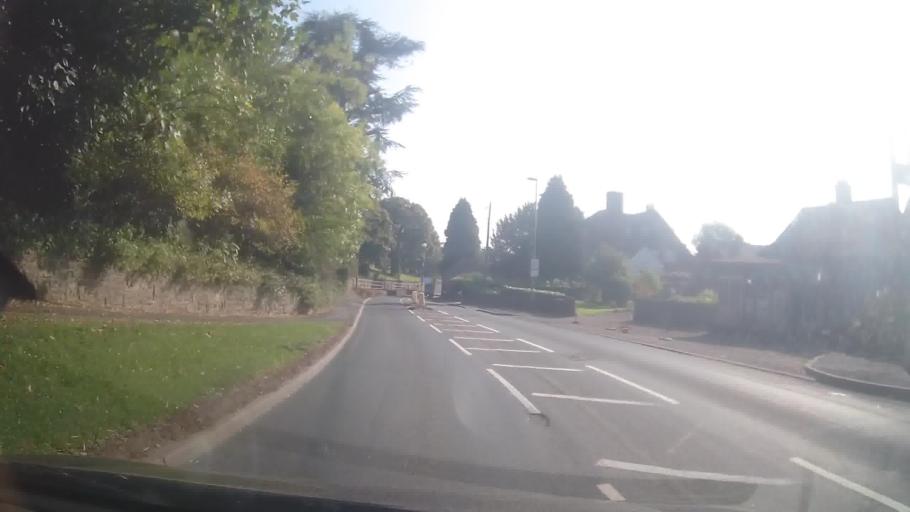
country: GB
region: England
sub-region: Shropshire
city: Much Wenlock
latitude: 52.5945
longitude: -2.5666
